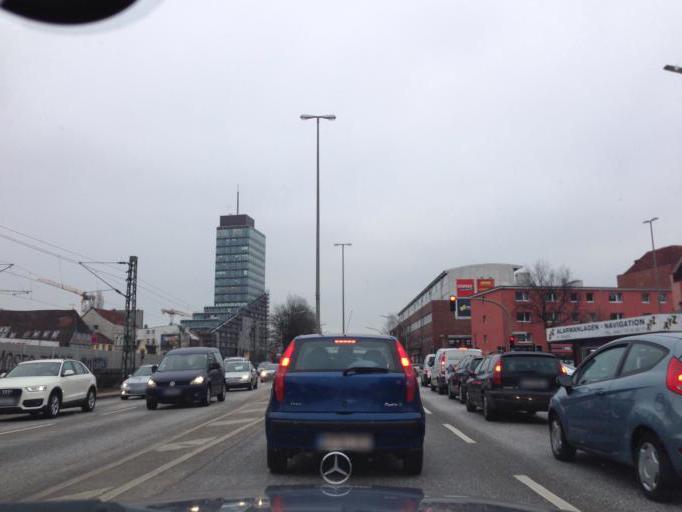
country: DE
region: Hamburg
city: Harburg
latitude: 53.4639
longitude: 9.9813
